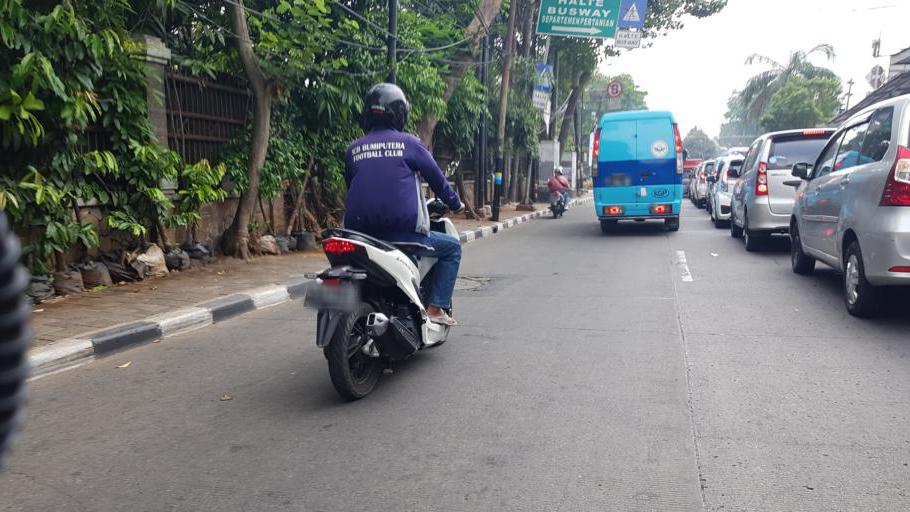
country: ID
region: Jakarta Raya
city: Jakarta
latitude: -6.2948
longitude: 106.8219
